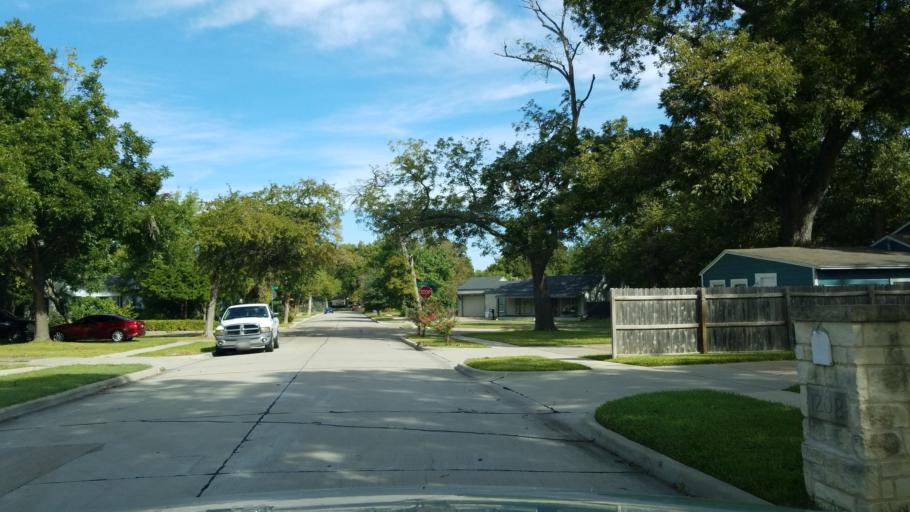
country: US
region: Texas
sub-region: Dallas County
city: Garland
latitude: 32.9027
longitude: -96.6519
